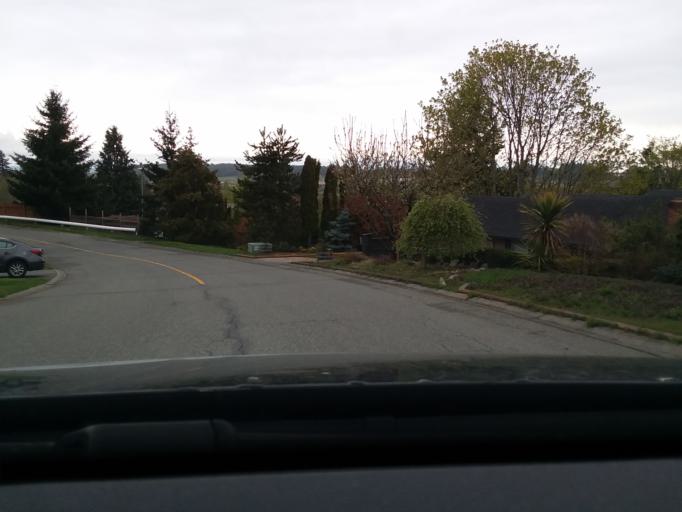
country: CA
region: British Columbia
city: North Saanich
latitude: 48.5620
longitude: -123.3975
